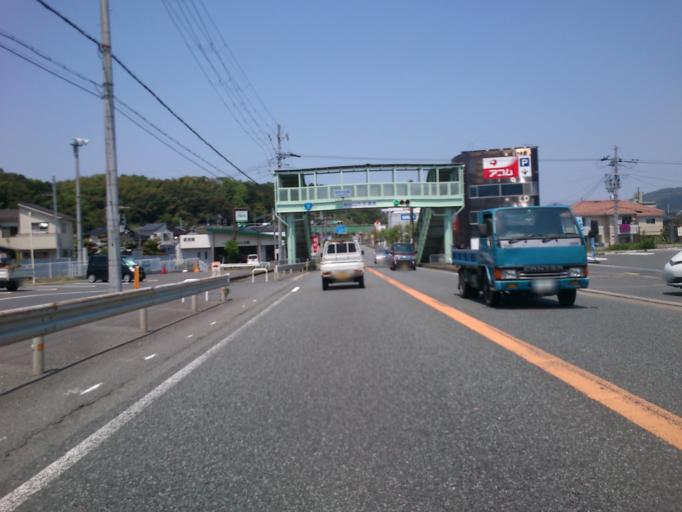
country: JP
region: Kyoto
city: Fukuchiyama
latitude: 35.2987
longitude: 135.1093
